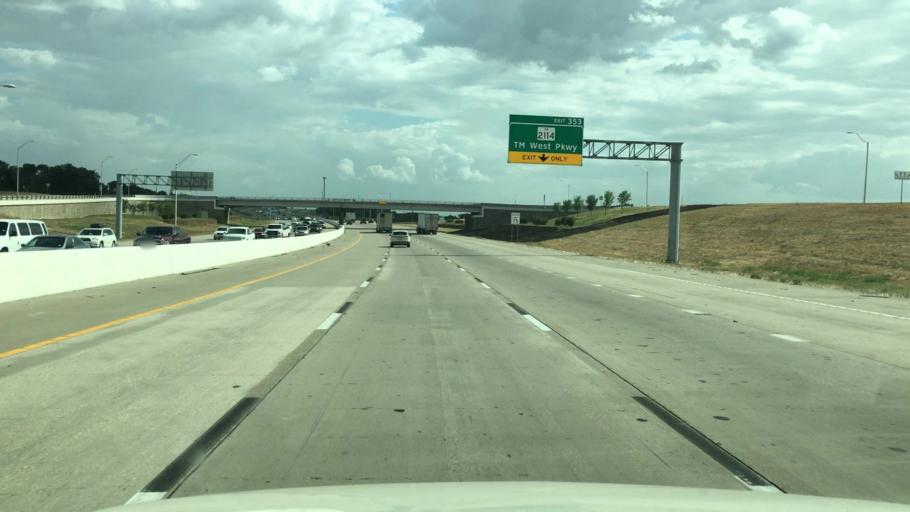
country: US
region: Texas
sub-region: McLennan County
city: West
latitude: 31.8214
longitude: -97.0975
